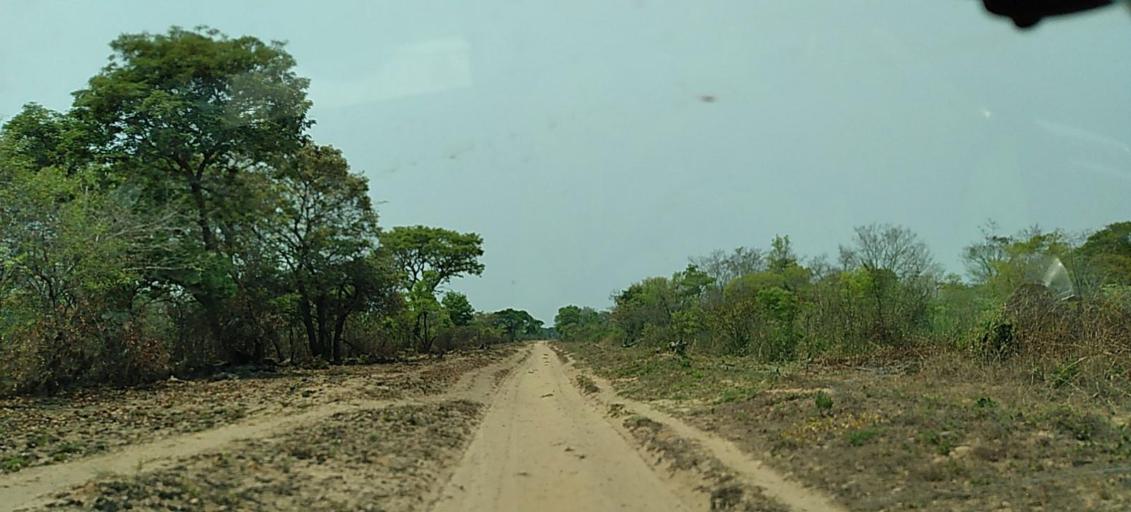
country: ZM
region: Western
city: Lukulu
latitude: -14.1514
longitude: 23.2983
